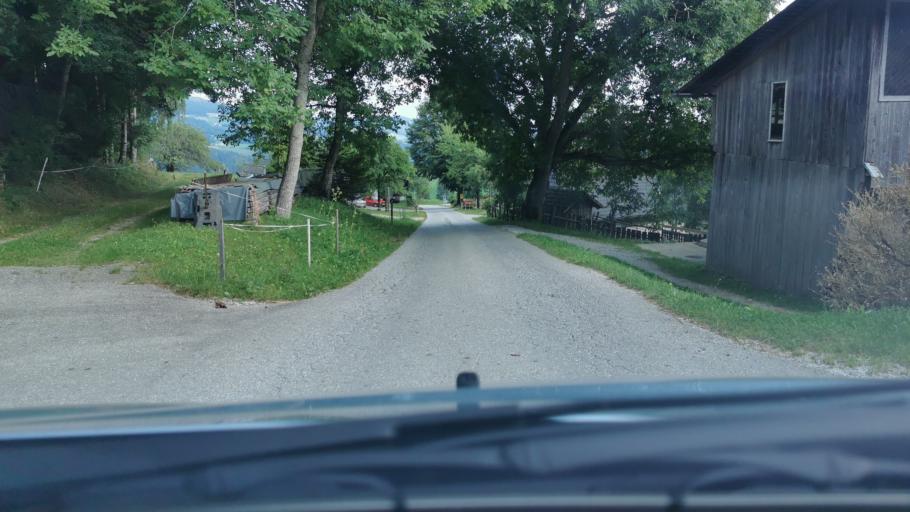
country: AT
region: Styria
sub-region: Politischer Bezirk Weiz
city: Koglhof
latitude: 47.3179
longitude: 15.6713
